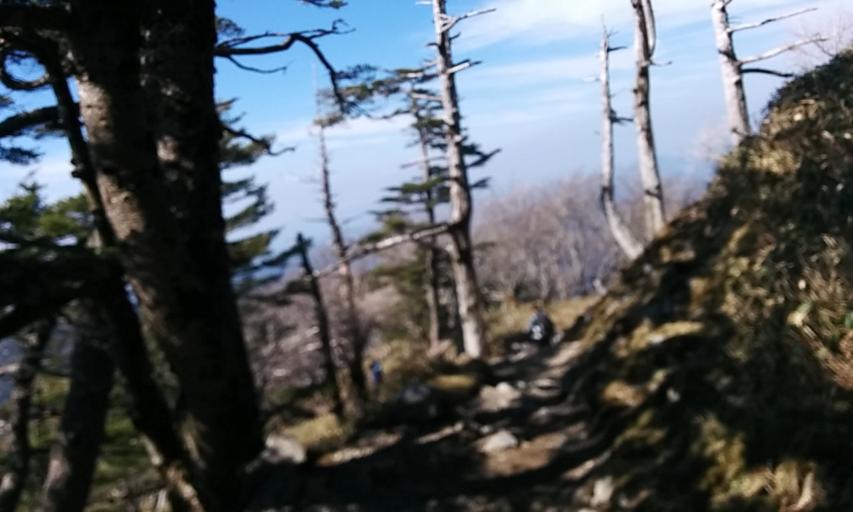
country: JP
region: Tokushima
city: Wakimachi
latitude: 33.8572
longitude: 134.0954
